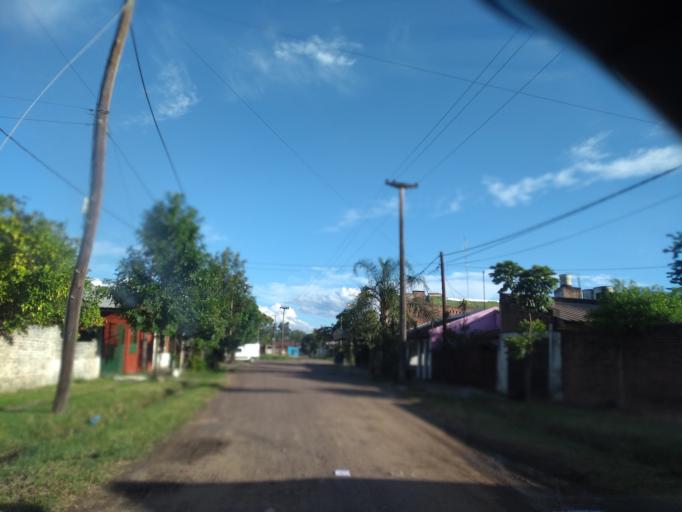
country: AR
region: Chaco
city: Fontana
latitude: -27.4139
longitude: -59.0349
